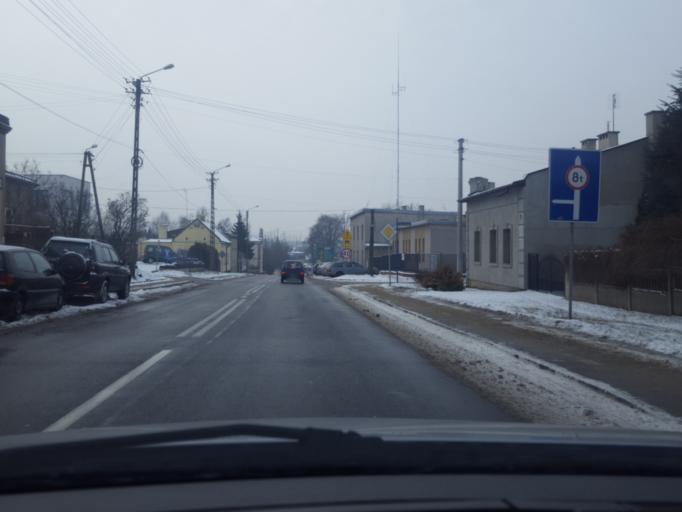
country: PL
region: Lodz Voivodeship
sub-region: Powiat brzezinski
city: Brzeziny
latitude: 51.8068
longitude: 19.7570
